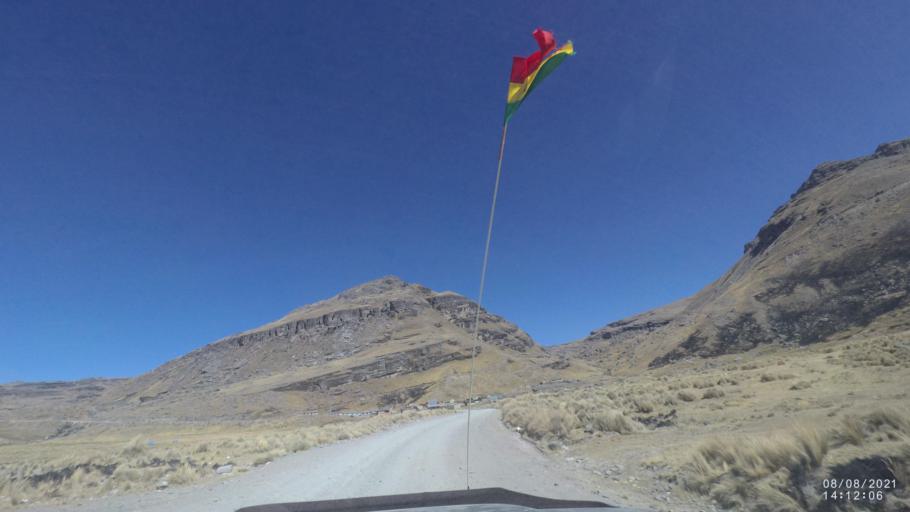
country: BO
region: Cochabamba
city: Sipe Sipe
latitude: -17.1630
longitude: -66.4288
